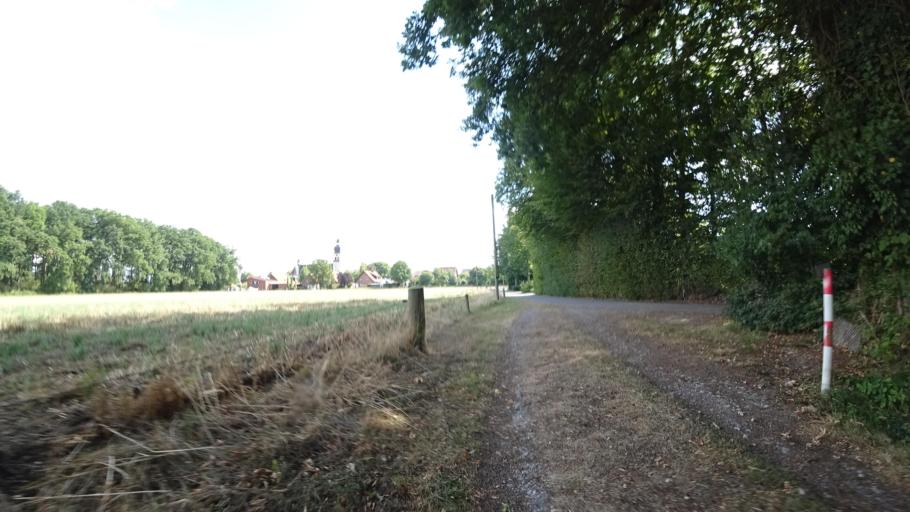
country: DE
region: North Rhine-Westphalia
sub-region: Regierungsbezirk Detmold
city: Rheda-Wiedenbruck
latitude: 51.8273
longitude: 8.2754
